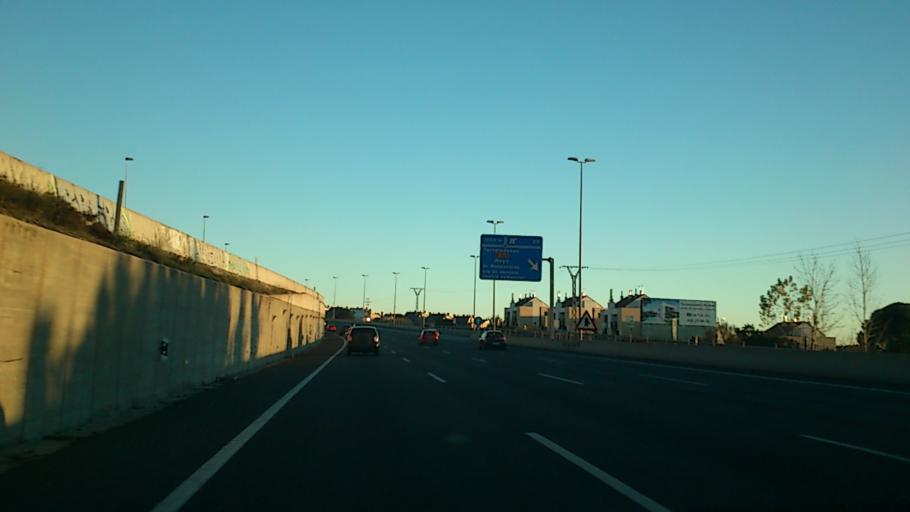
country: ES
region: Madrid
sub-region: Provincia de Madrid
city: Torrelodones
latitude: 40.5809
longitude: -3.9478
